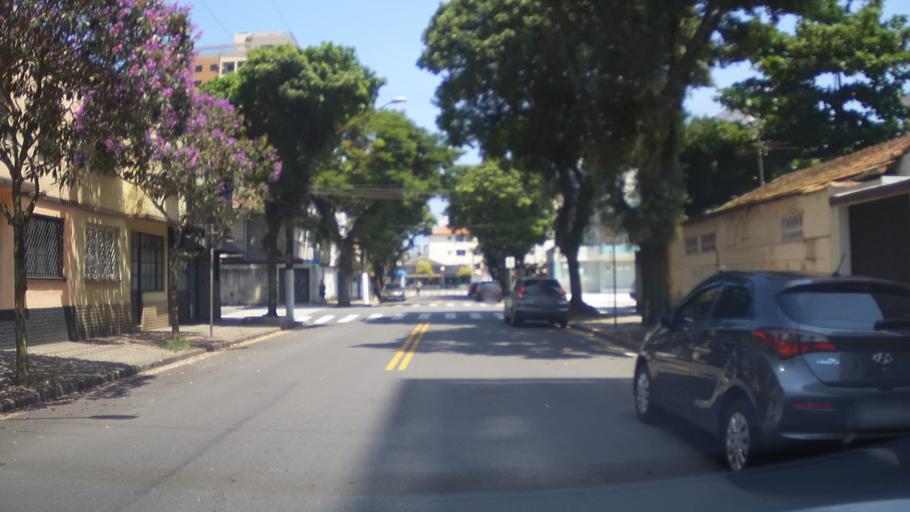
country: BR
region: Sao Paulo
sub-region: Santos
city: Santos
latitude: -23.9738
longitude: -46.3032
